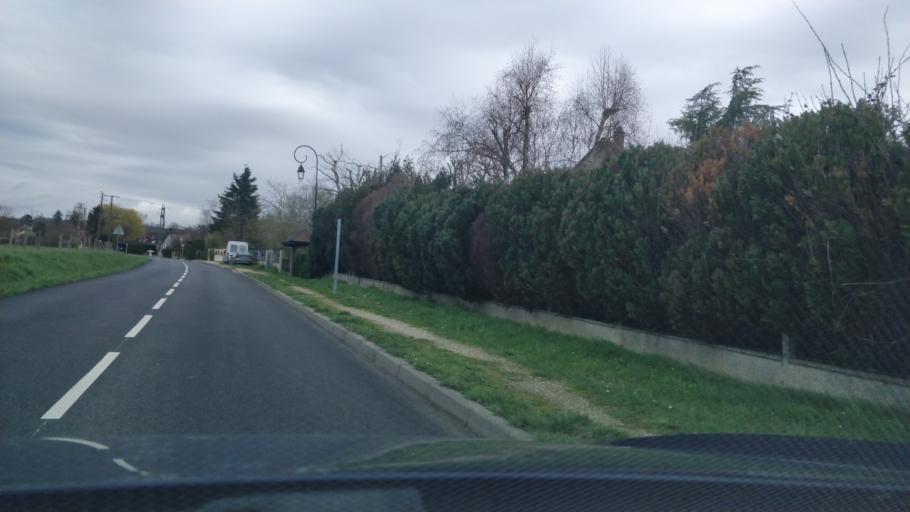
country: FR
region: Ile-de-France
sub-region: Departement de l'Essonne
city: Vaugrigneuse
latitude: 48.5969
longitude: 2.1177
